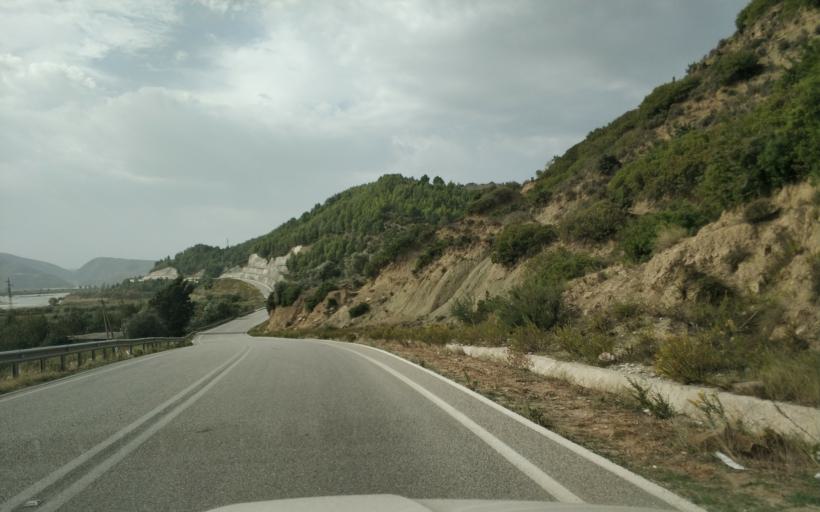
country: AL
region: Gjirokaster
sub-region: Rrethi i Tepelenes
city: Luftinje
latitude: 40.3807
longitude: 19.9019
